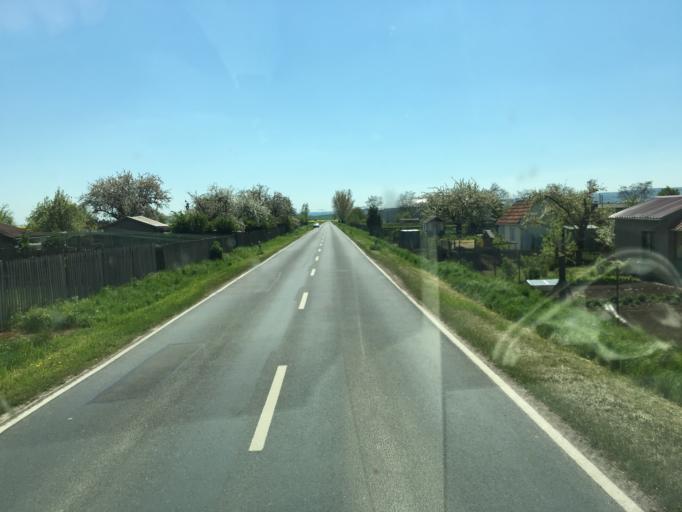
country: DE
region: Thuringia
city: Heygendorf
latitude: 51.3518
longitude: 11.3669
